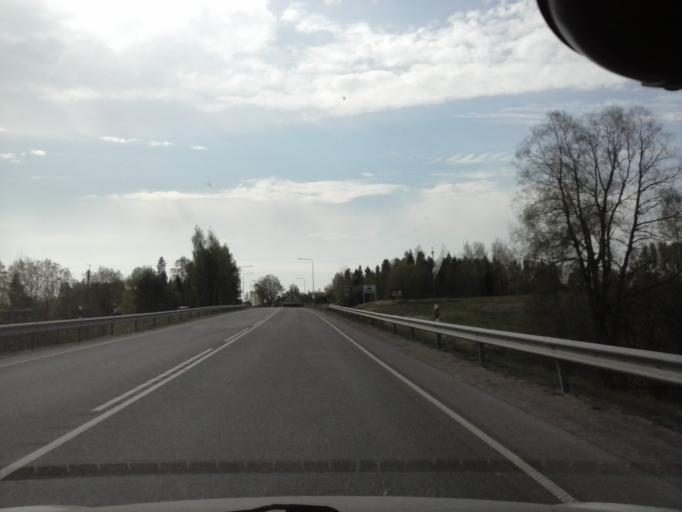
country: EE
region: Tartu
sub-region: UElenurme vald
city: Ulenurme
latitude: 58.1487
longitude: 26.6978
